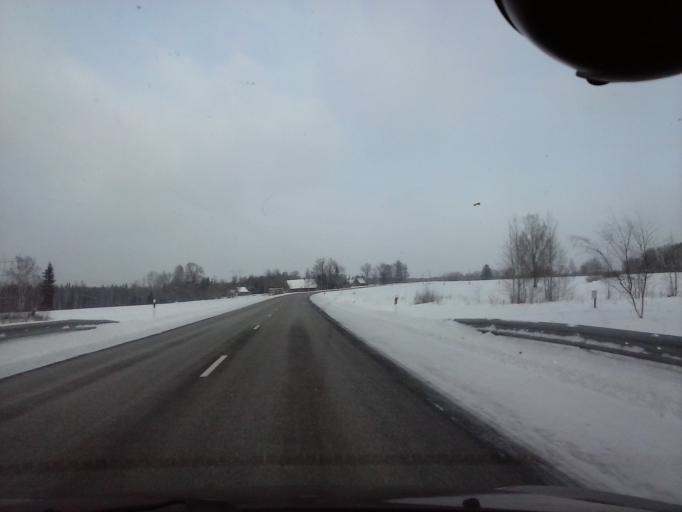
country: EE
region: Paernumaa
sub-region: Saarde vald
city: Kilingi-Nomme
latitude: 58.1733
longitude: 25.0335
